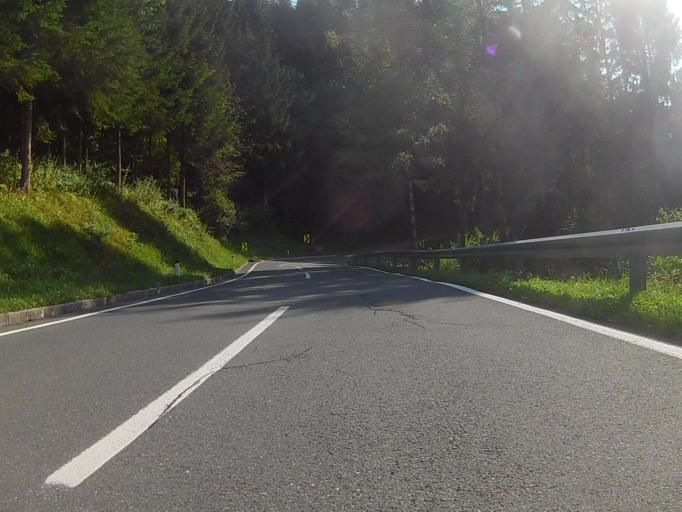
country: AT
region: Carinthia
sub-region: Politischer Bezirk Wolfsberg
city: Lavamund
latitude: 46.6534
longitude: 14.9819
